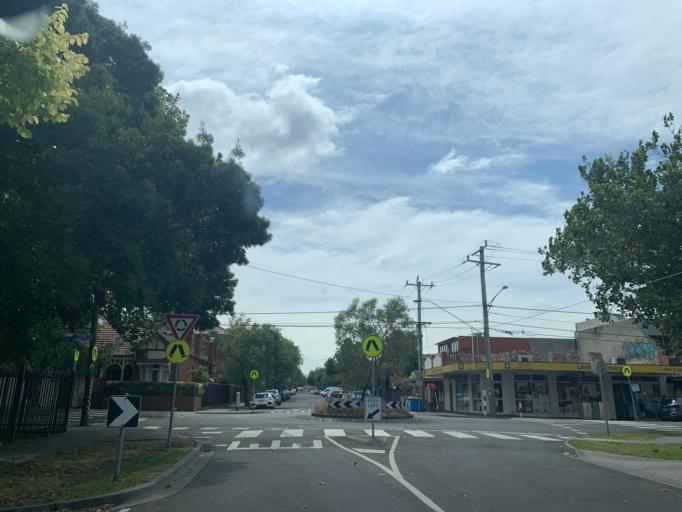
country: AU
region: Victoria
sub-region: Port Phillip
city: Elwood
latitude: -37.8803
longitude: 144.9907
